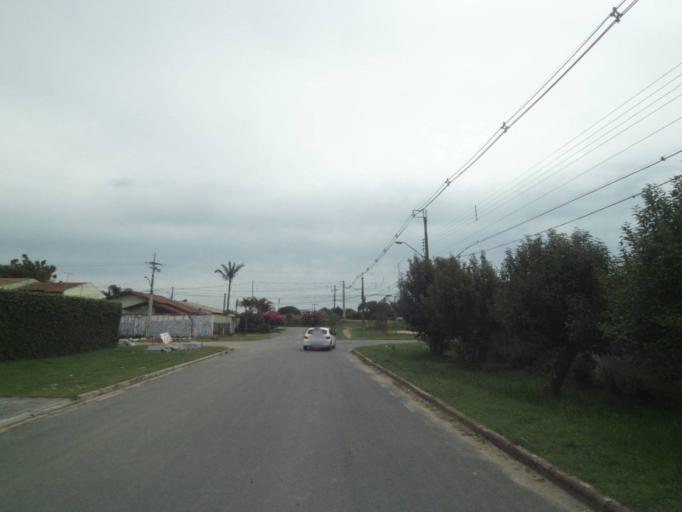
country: BR
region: Parana
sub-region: Pinhais
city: Pinhais
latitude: -25.4288
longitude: -49.2035
